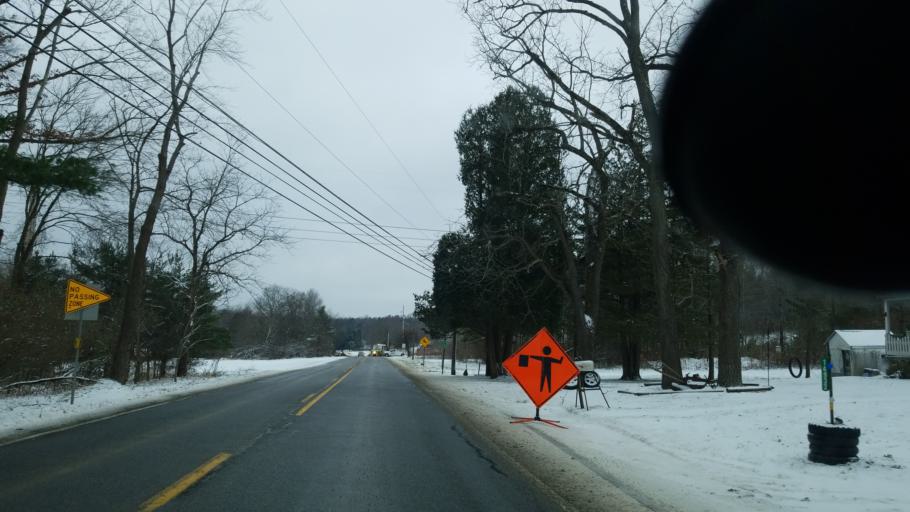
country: US
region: Pennsylvania
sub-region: Indiana County
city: Johnsonburg
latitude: 40.9276
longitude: -78.8959
